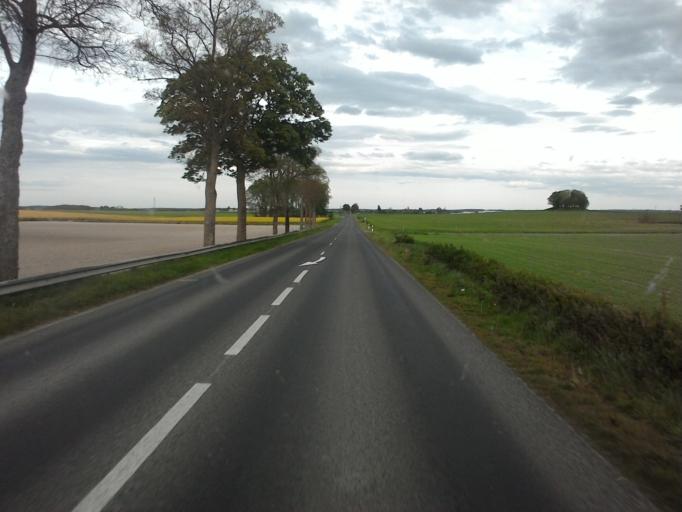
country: FR
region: Champagne-Ardenne
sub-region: Departement des Ardennes
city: Vouziers
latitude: 49.3927
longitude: 4.6593
